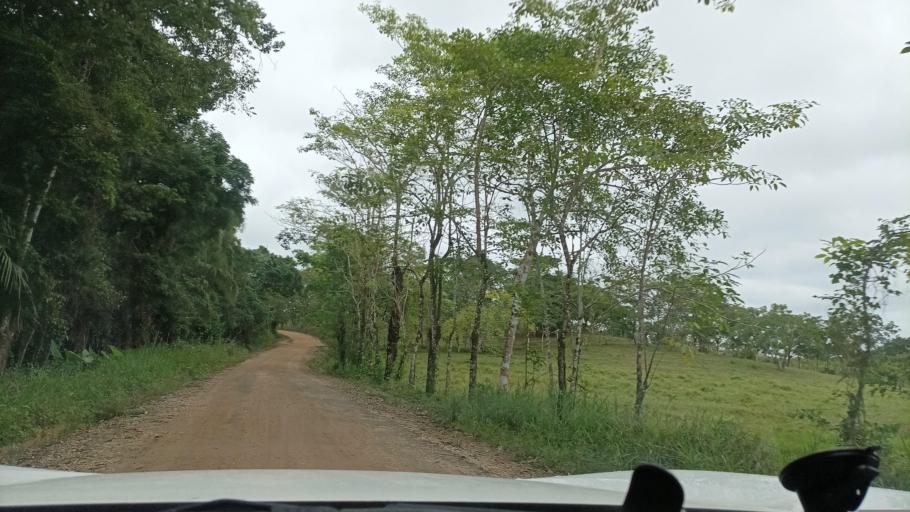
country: MX
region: Veracruz
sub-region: Moloacan
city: Cuichapa
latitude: 17.7897
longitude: -94.3657
